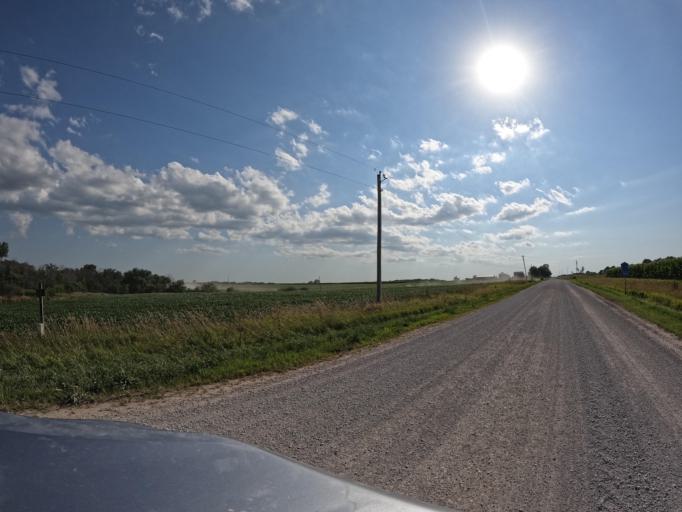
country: US
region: Iowa
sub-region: Appanoose County
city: Centerville
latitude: 40.7179
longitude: -93.0384
